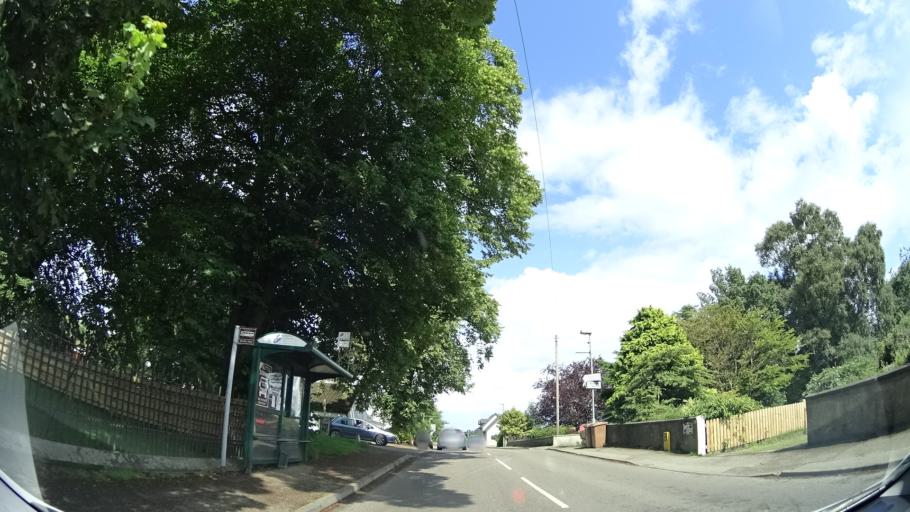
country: GB
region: Scotland
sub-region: Highland
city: Fortrose
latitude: 57.5829
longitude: -4.1285
